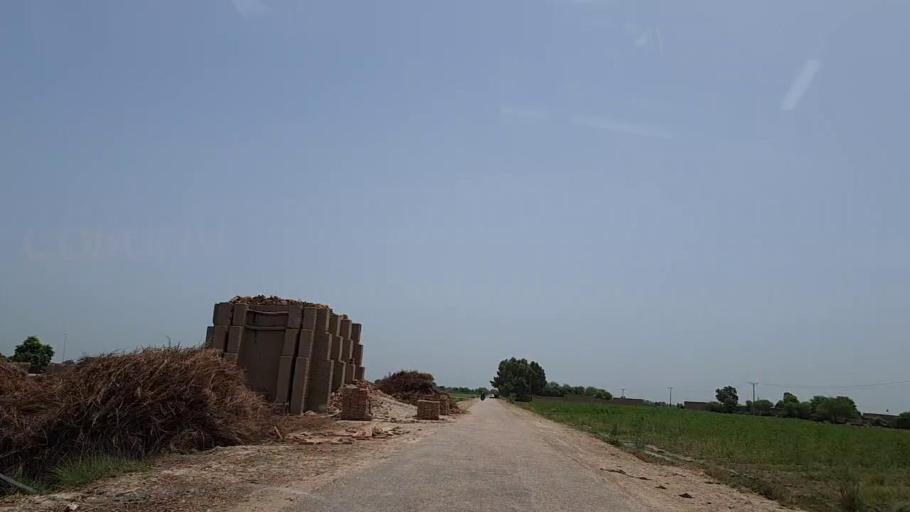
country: PK
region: Sindh
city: Tharu Shah
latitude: 26.9624
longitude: 68.0577
